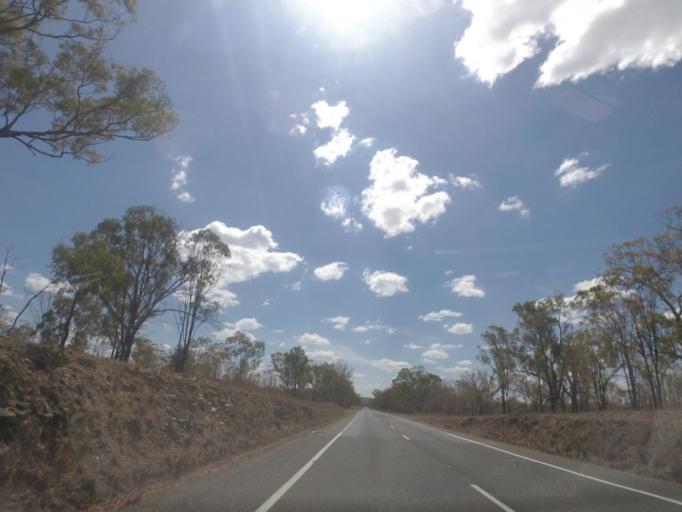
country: AU
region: Queensland
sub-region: Southern Downs
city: Warwick
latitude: -28.1650
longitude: 151.7201
